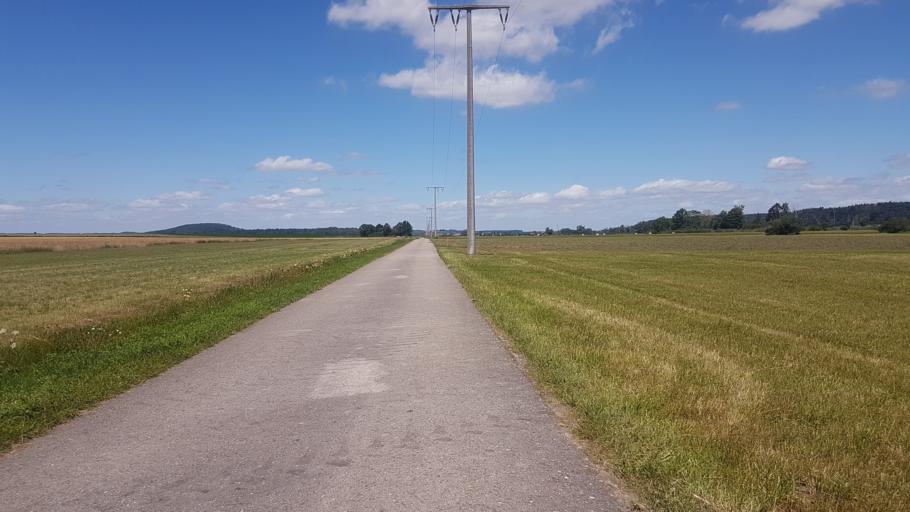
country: DE
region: Bavaria
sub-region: Regierungsbezirk Mittelfranken
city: Aurach
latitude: 49.2632
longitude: 10.4503
